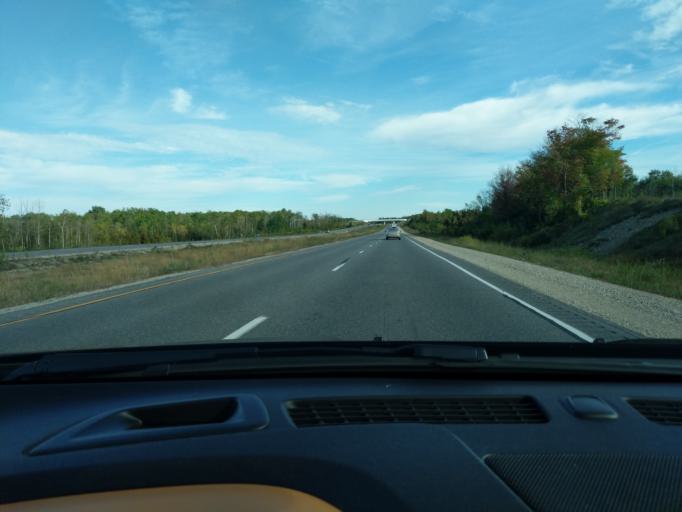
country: CA
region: Ontario
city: Collingwood
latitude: 44.4746
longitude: -80.1515
